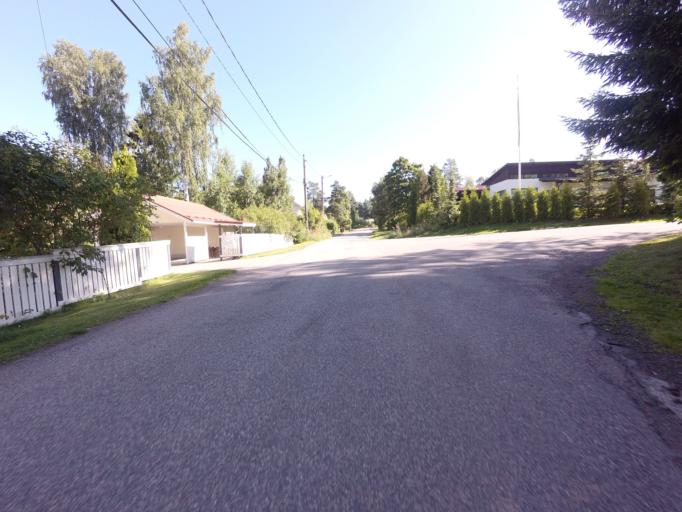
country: FI
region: Uusimaa
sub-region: Helsinki
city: Espoo
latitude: 60.1622
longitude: 24.6709
